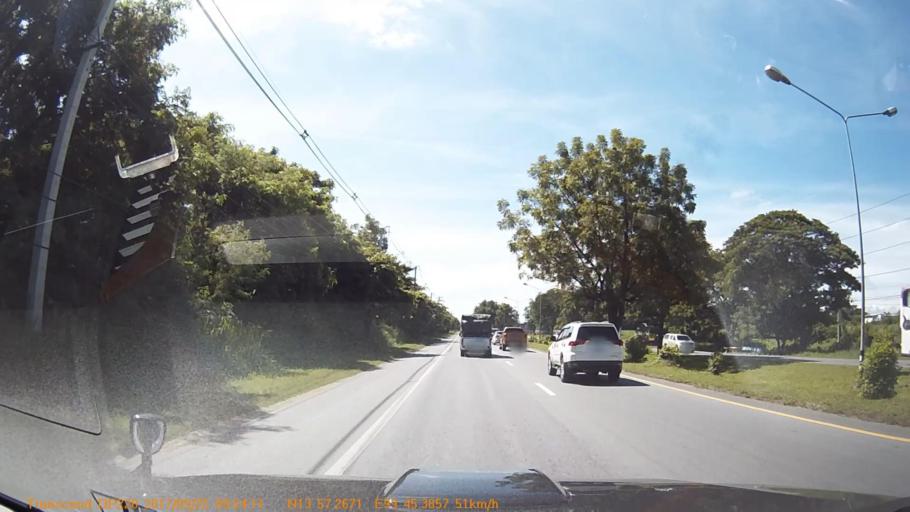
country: TH
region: Kanchanaburi
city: Tha Maka
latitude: 13.9543
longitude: 99.7565
